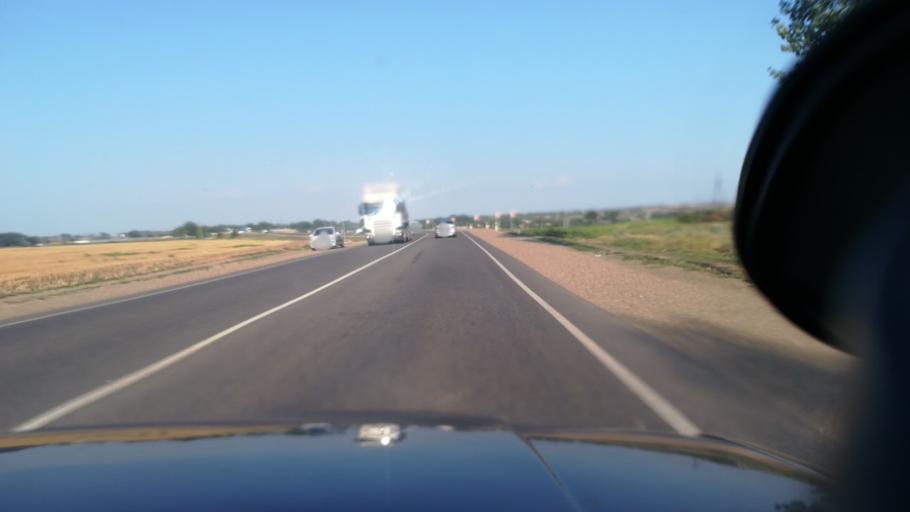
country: RU
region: Krasnodarskiy
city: Yurovka
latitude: 45.1188
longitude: 37.3828
